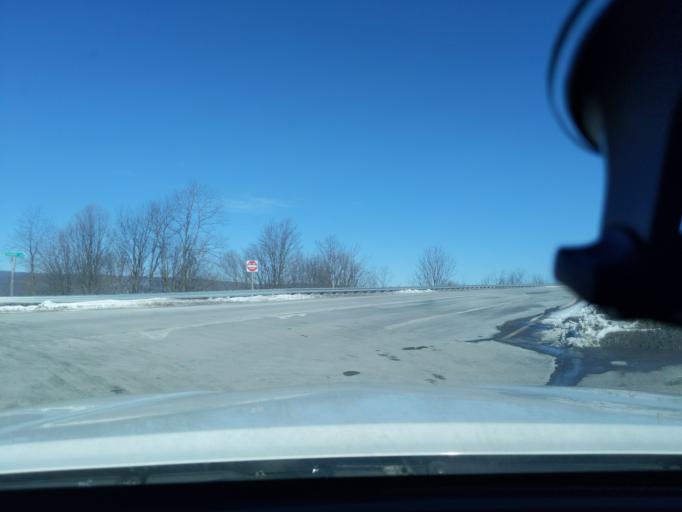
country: US
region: Maryland
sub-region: Allegany County
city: Frostburg
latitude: 39.6361
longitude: -78.9177
